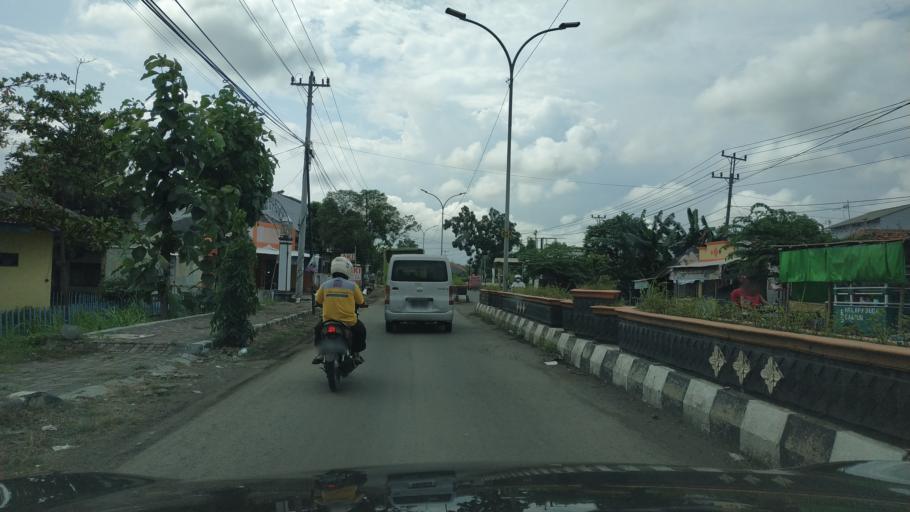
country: ID
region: Central Java
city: Pemalang
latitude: -6.9253
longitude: 109.3861
